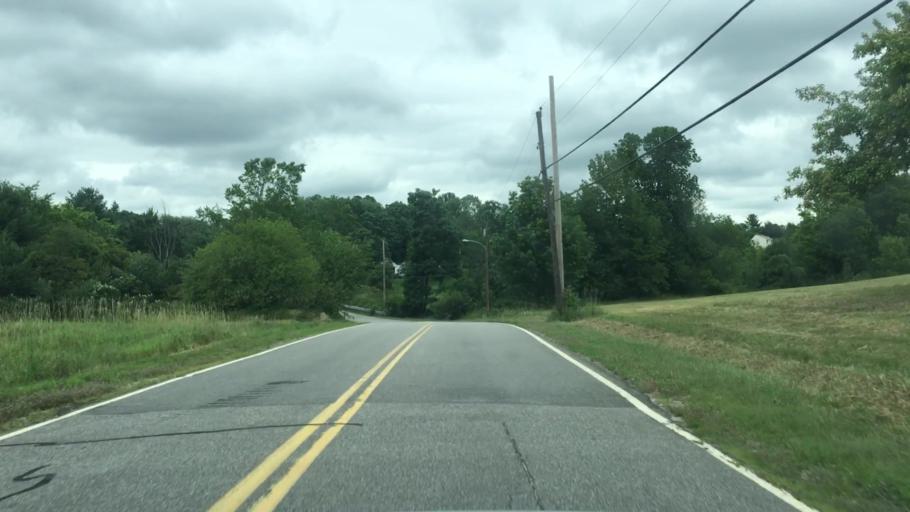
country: US
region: Maine
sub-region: York County
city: Biddeford
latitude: 43.5178
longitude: -70.5130
